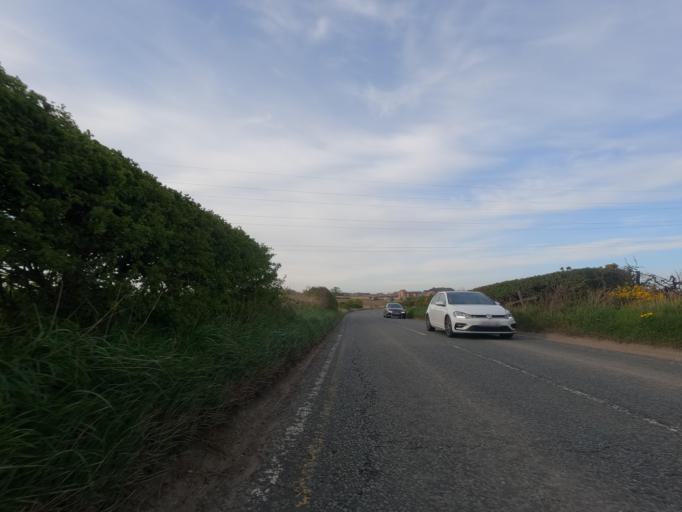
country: GB
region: England
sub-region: Newcastle upon Tyne
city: Hazlerigg
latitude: 55.0247
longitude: -1.6652
